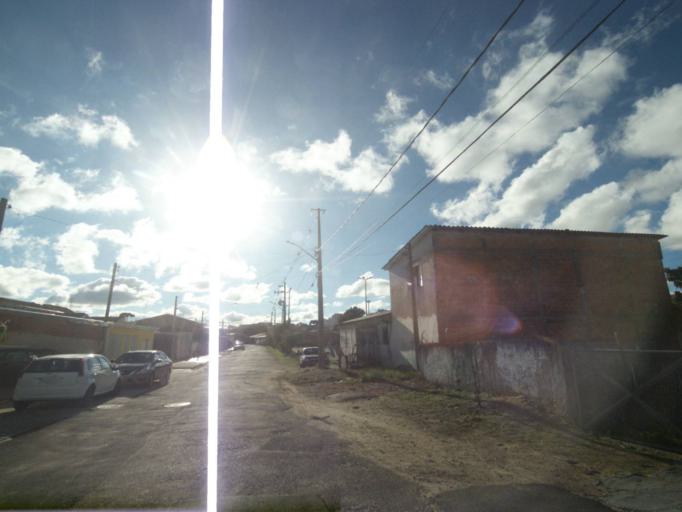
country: BR
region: Parana
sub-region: Sao Jose Dos Pinhais
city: Sao Jose dos Pinhais
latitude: -25.5233
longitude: -49.2808
